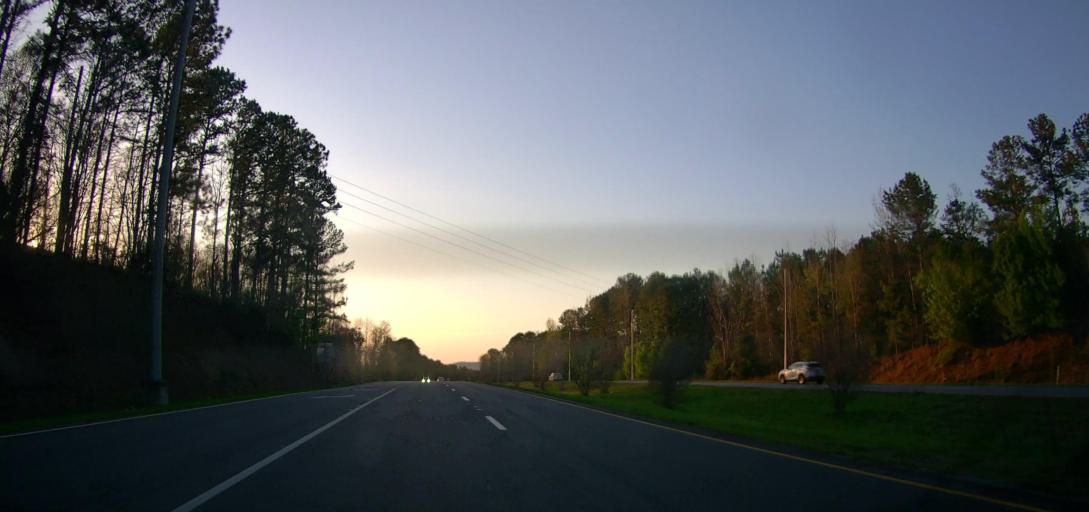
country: US
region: Alabama
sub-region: Talladega County
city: Sylacauga
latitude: 33.1457
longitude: -86.2603
